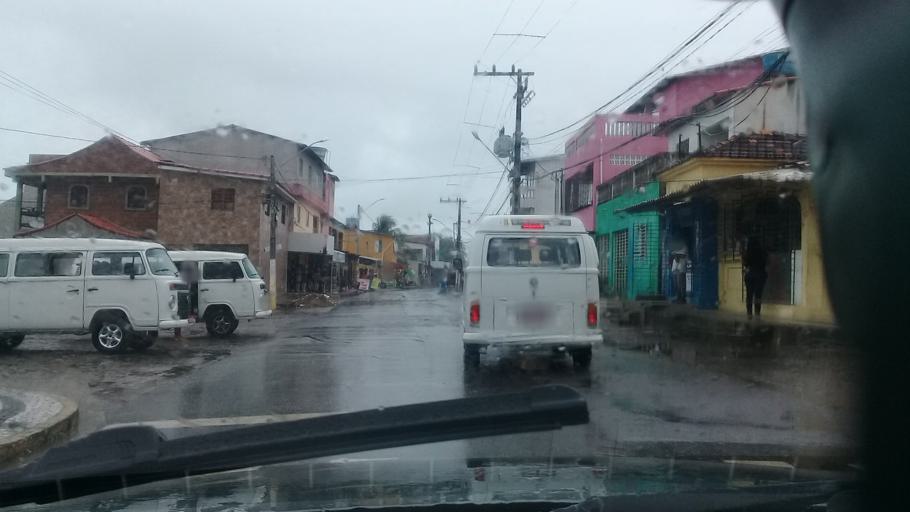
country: BR
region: Pernambuco
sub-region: Itamaraca
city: Itamaraca
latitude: -7.7327
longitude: -34.8259
